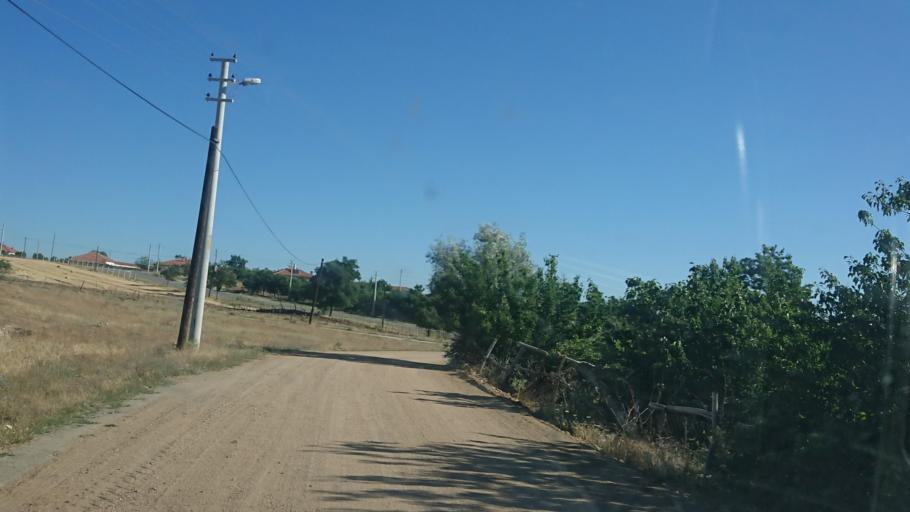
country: TR
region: Aksaray
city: Agacoren
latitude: 38.8763
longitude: 33.9522
